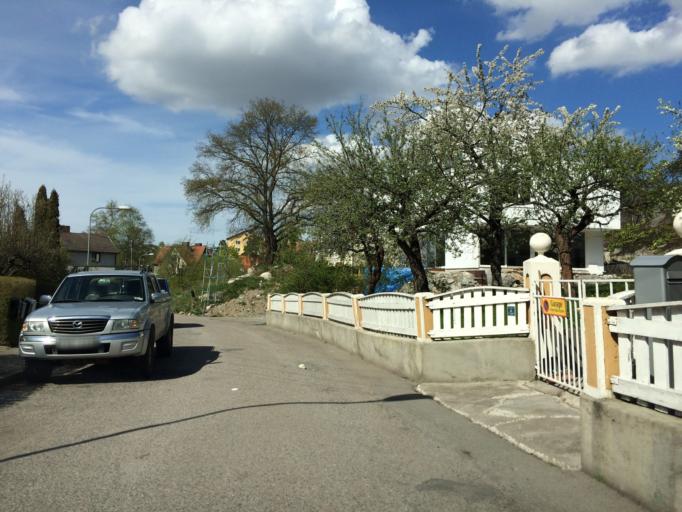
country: SE
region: Stockholm
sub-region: Huddinge Kommun
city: Segeltorp
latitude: 59.3021
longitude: 17.9602
